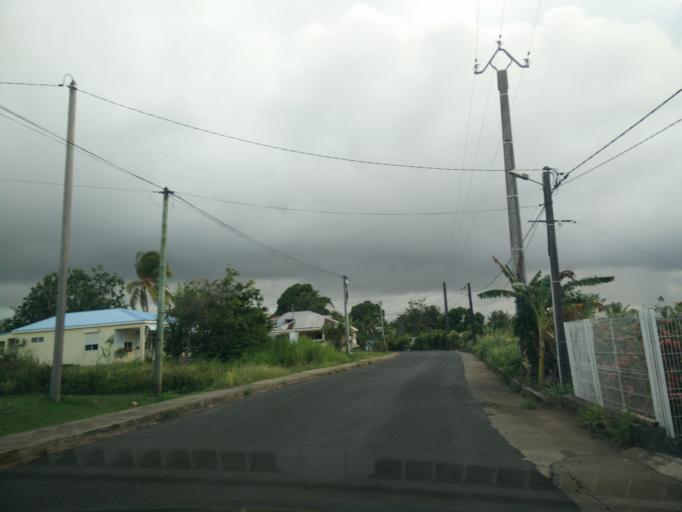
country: GP
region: Guadeloupe
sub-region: Guadeloupe
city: Petit-Bourg
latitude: 16.1884
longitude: -61.6135
